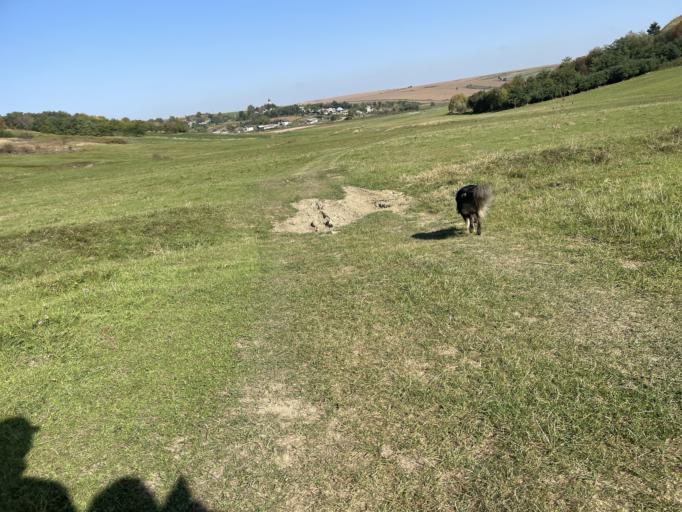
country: RO
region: Iasi
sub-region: Comuna Dumesti
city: Pausesti
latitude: 47.1556
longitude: 27.3086
